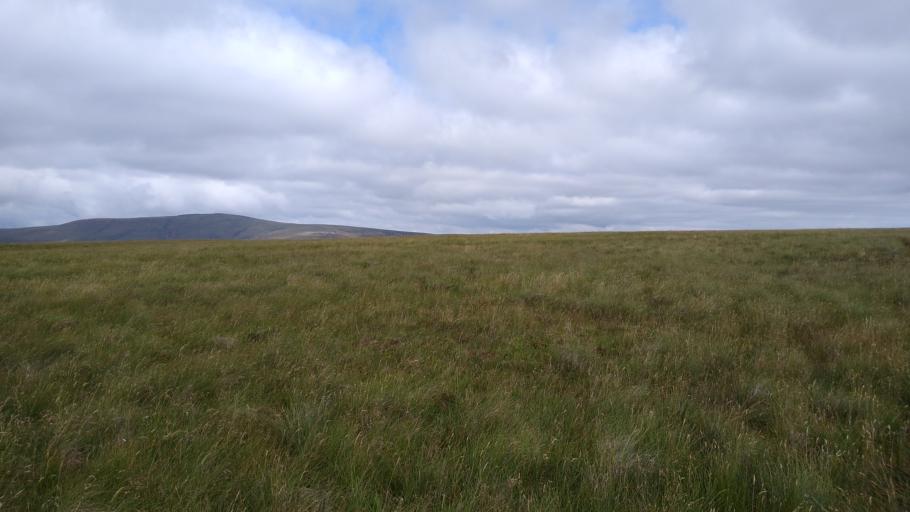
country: GB
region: England
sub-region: Cumbria
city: Keswick
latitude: 54.6527
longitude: -3.0713
